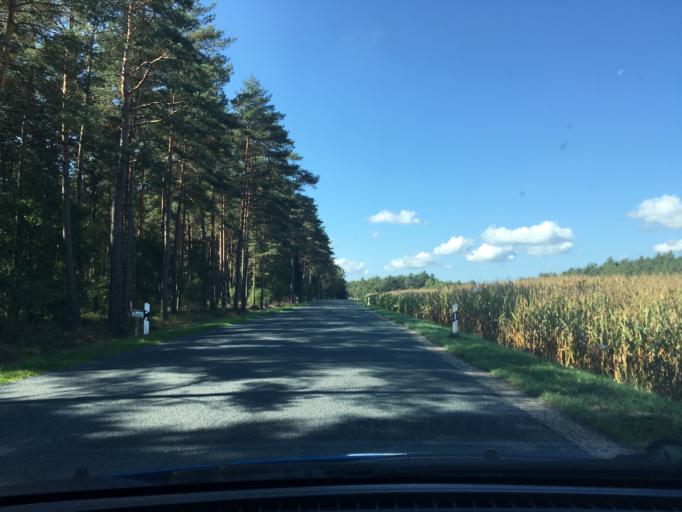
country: DE
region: Lower Saxony
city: Wietzendorf
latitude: 52.8921
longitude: 10.0217
